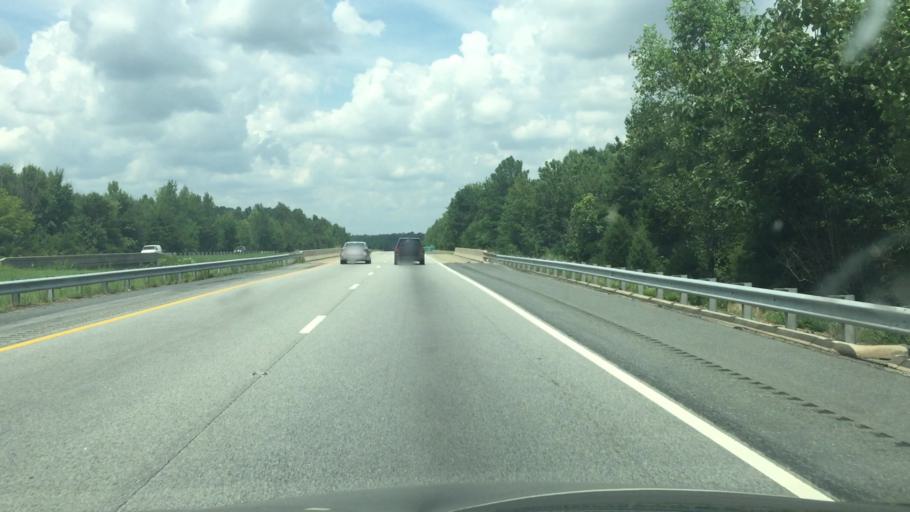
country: US
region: North Carolina
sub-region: Guilford County
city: Pleasant Garden
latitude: 35.9658
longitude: -79.8206
